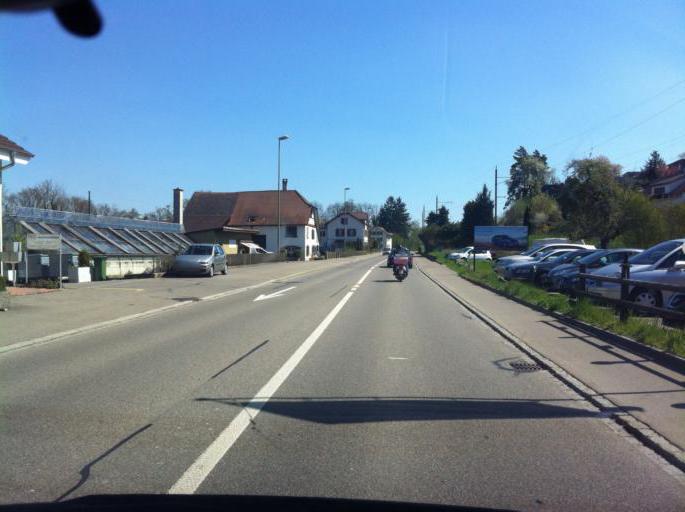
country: CH
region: Zurich
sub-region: Bezirk Andelfingen
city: Feuerthalen
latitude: 47.6839
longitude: 8.6643
